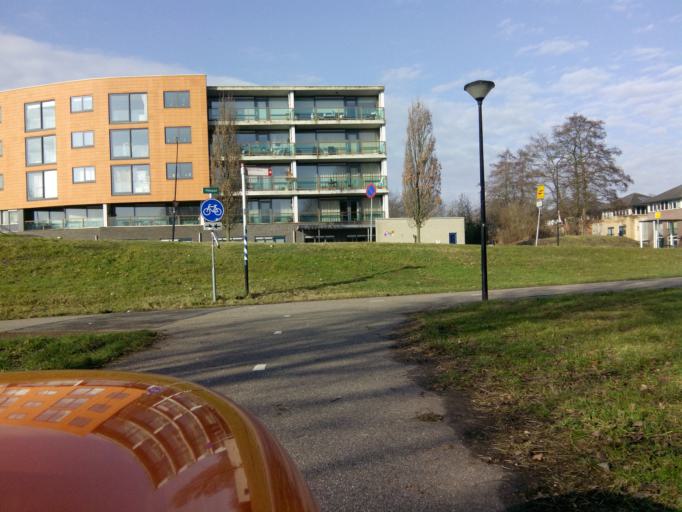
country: NL
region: Utrecht
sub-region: Gemeente Leusden
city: Leusden
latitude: 52.1429
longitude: 5.4302
